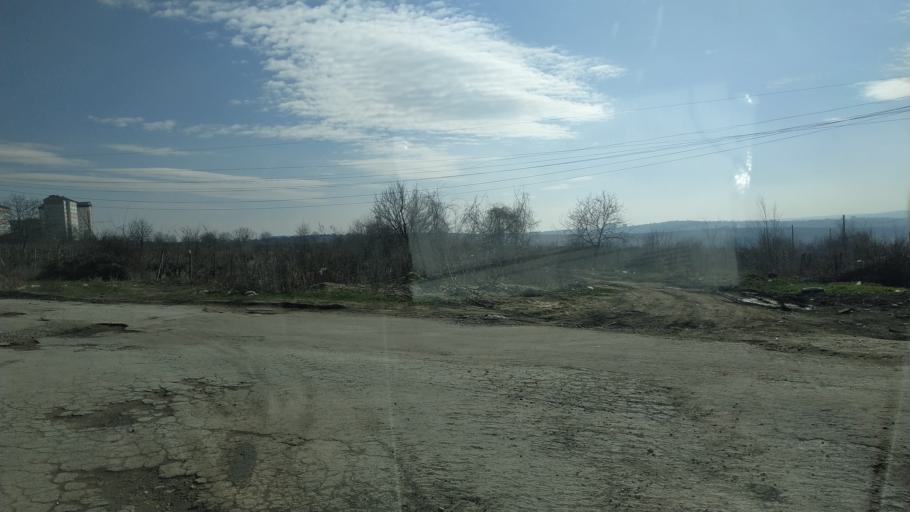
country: MD
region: Chisinau
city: Vatra
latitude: 47.0146
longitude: 28.7415
